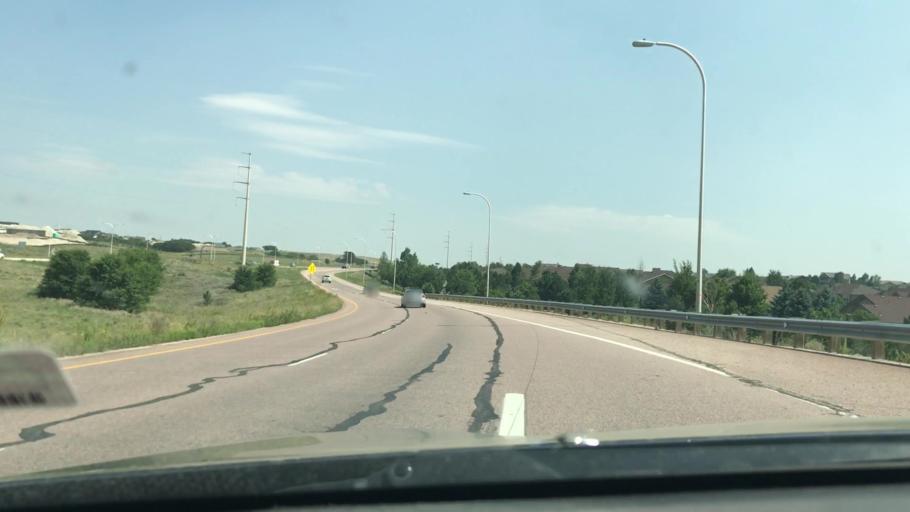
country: US
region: Colorado
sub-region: El Paso County
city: Black Forest
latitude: 38.9832
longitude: -104.7647
